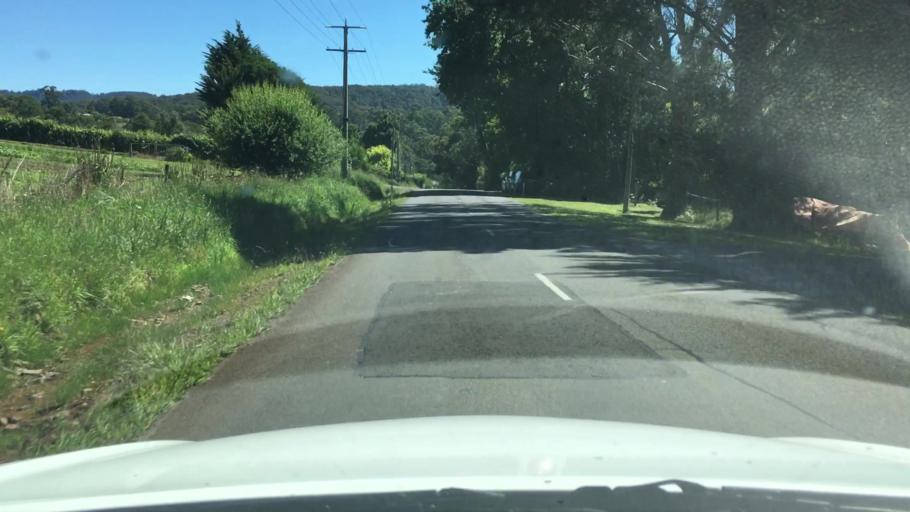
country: AU
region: Victoria
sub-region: Yarra Ranges
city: Mount Evelyn
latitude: -37.8023
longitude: 145.4151
